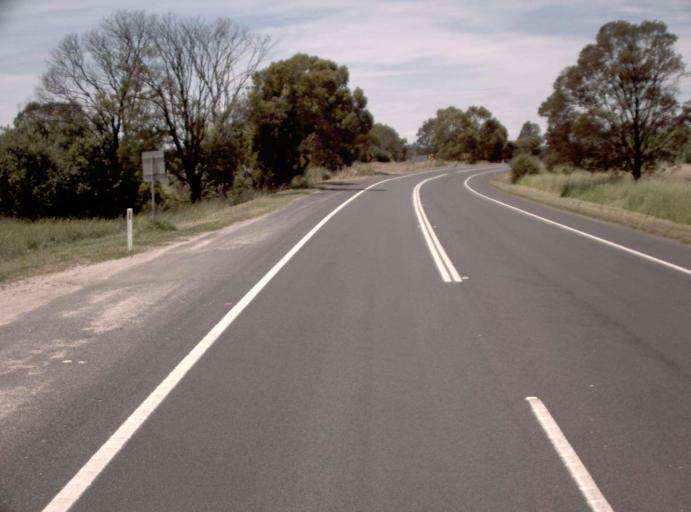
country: AU
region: Victoria
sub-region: Latrobe
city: Traralgon
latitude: -38.1590
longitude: 146.7081
